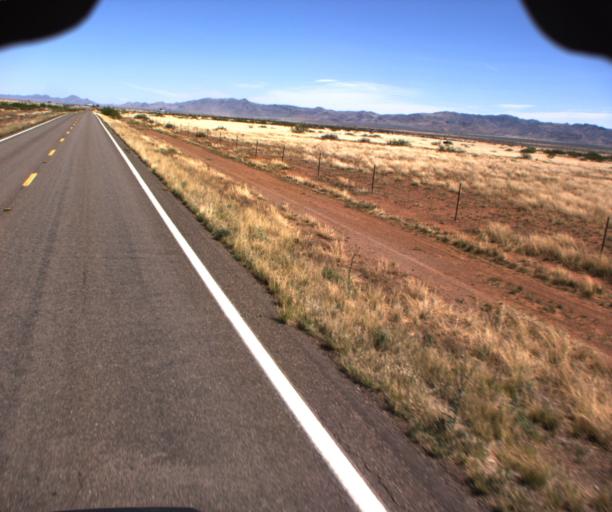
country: US
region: Arizona
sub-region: Cochise County
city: Douglas
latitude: 31.6739
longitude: -109.1443
